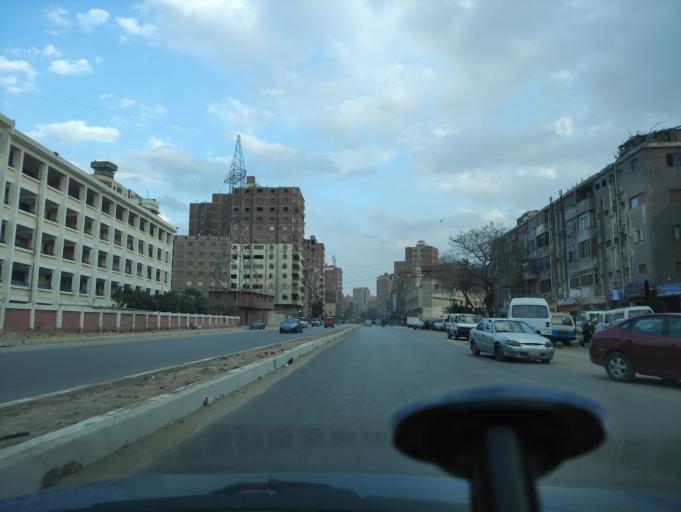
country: EG
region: Muhafazat al Qalyubiyah
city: Al Khankah
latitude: 30.1338
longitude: 31.3573
